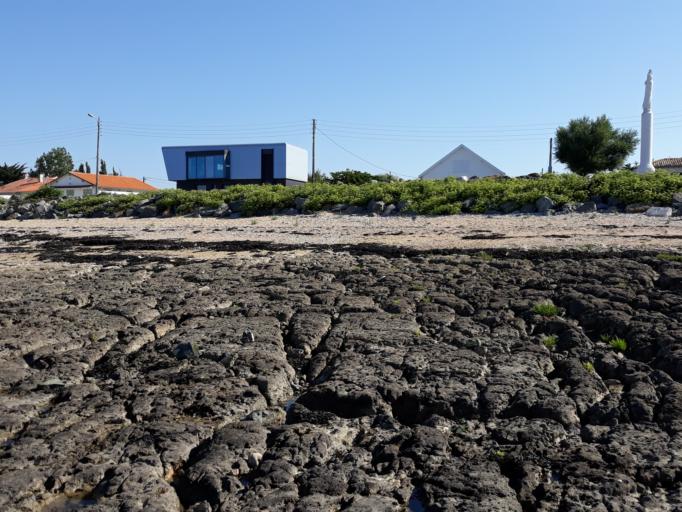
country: FR
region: Poitou-Charentes
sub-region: Departement de la Charente-Maritime
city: Fouras
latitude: 45.9998
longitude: -1.1120
